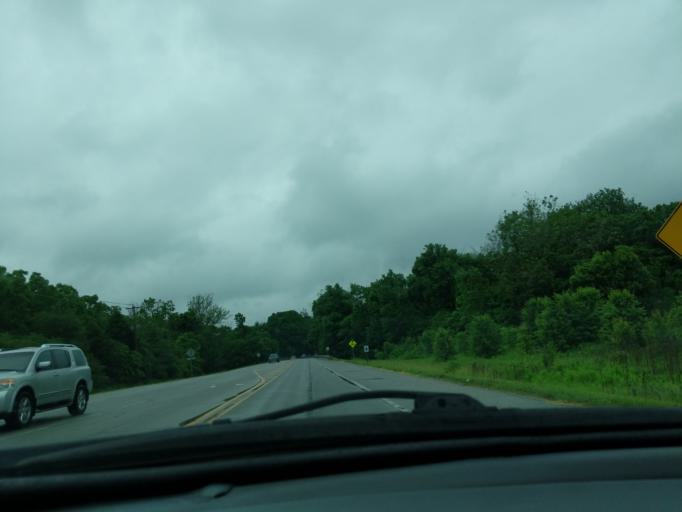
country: US
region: Indiana
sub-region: Hamilton County
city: Noblesville
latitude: 40.0554
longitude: -86.0393
